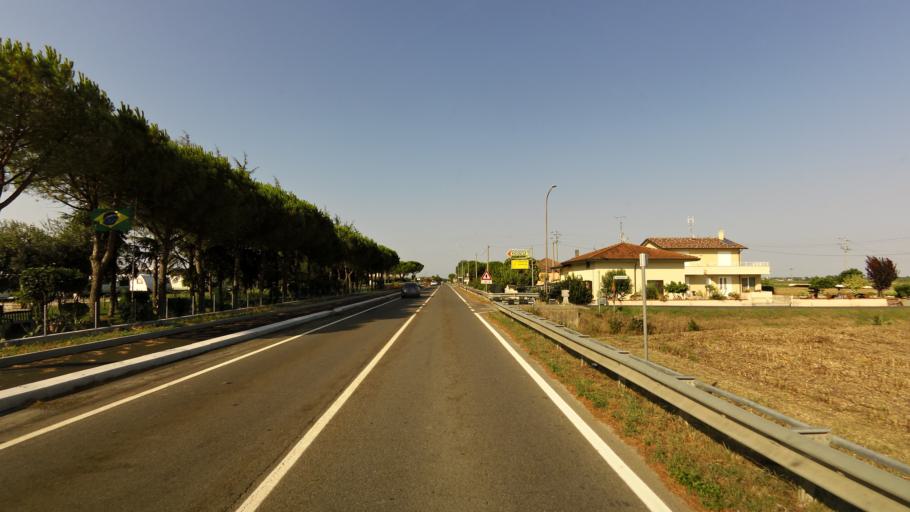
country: IT
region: Emilia-Romagna
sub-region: Provincia di Ravenna
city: Cervia
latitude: 44.2167
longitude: 12.3364
